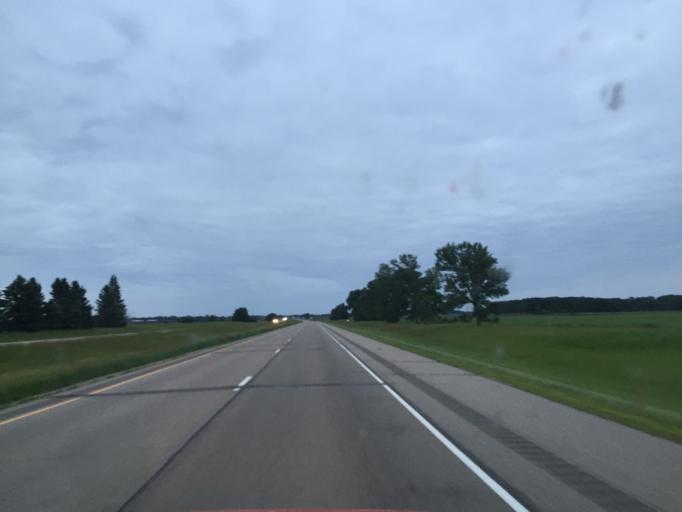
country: US
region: Minnesota
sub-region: Mower County
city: Austin
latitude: 43.6597
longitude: -93.0649
